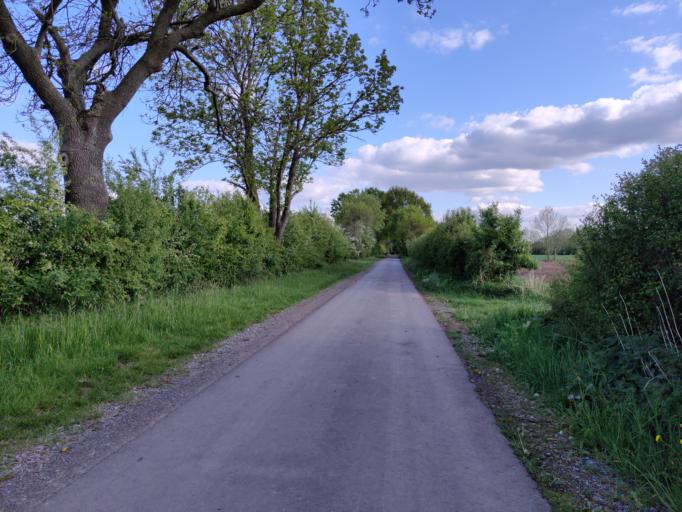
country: DE
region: Lower Saxony
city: Wunstorf
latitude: 52.4389
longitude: 9.4759
